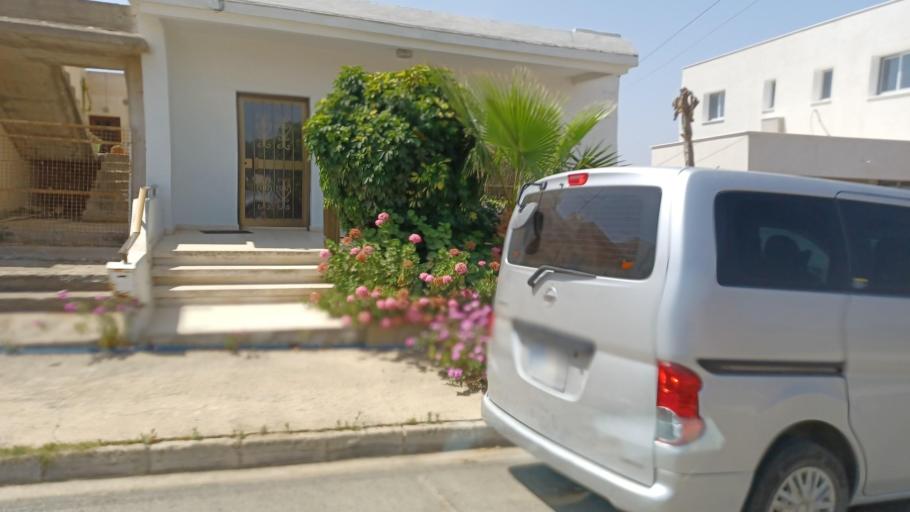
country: CY
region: Ammochostos
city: Paralimni
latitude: 35.0505
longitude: 33.9799
